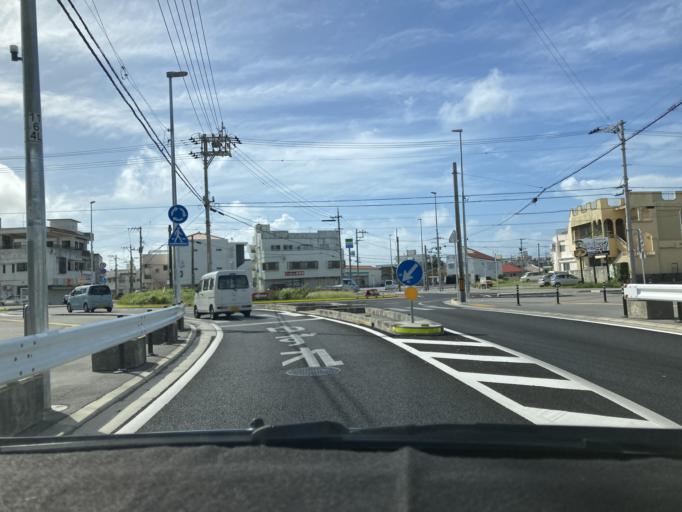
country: JP
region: Okinawa
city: Itoman
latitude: 26.1298
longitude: 127.6698
